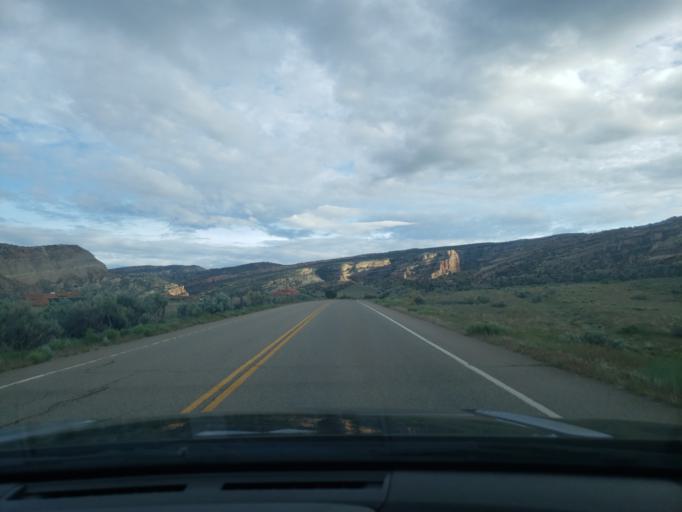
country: US
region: Colorado
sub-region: Mesa County
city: Redlands
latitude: 39.0400
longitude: -108.6286
